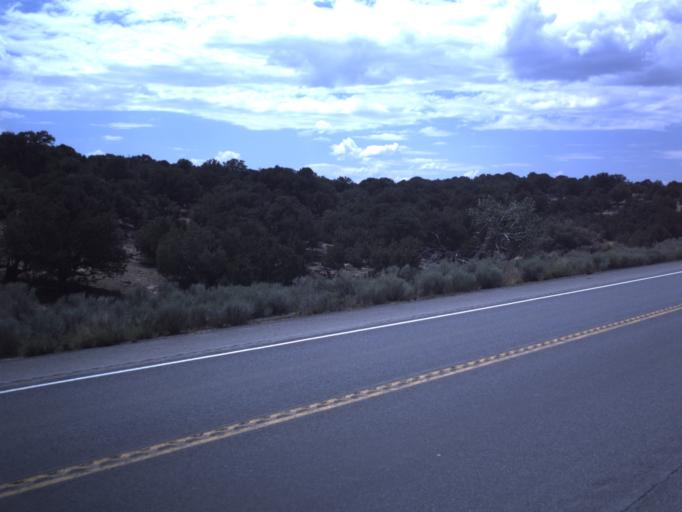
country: US
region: Utah
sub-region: Duchesne County
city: Duchesne
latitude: 40.1782
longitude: -110.5129
